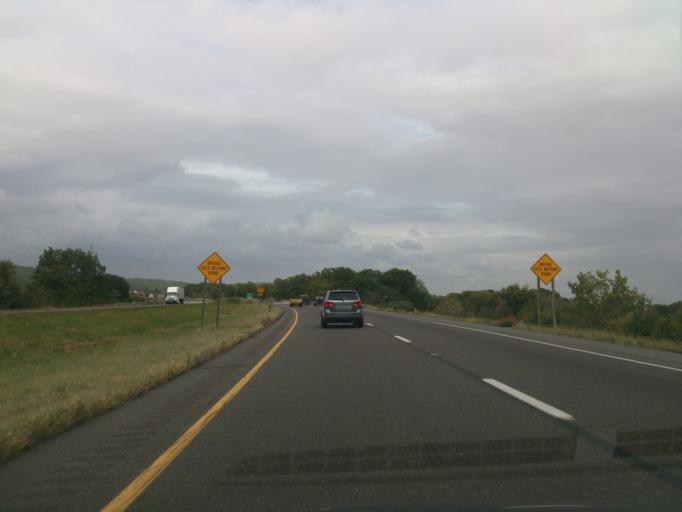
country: US
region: Pennsylvania
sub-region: Lancaster County
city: Ephrata
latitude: 40.1558
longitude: -76.1555
